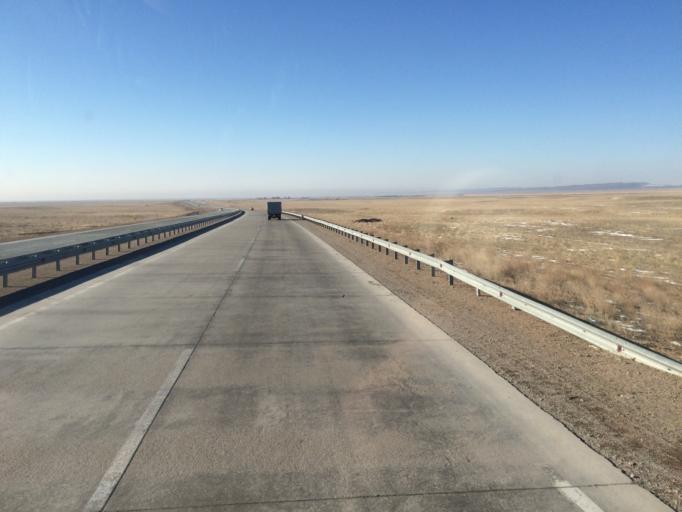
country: KZ
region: Zhambyl
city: Georgiyevka
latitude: 43.3428
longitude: 74.4442
